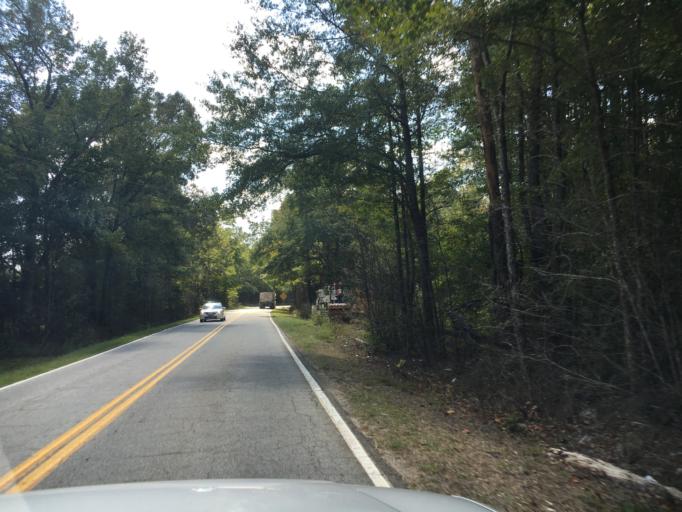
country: US
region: South Carolina
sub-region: Spartanburg County
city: Woodruff
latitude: 34.6981
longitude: -82.0526
